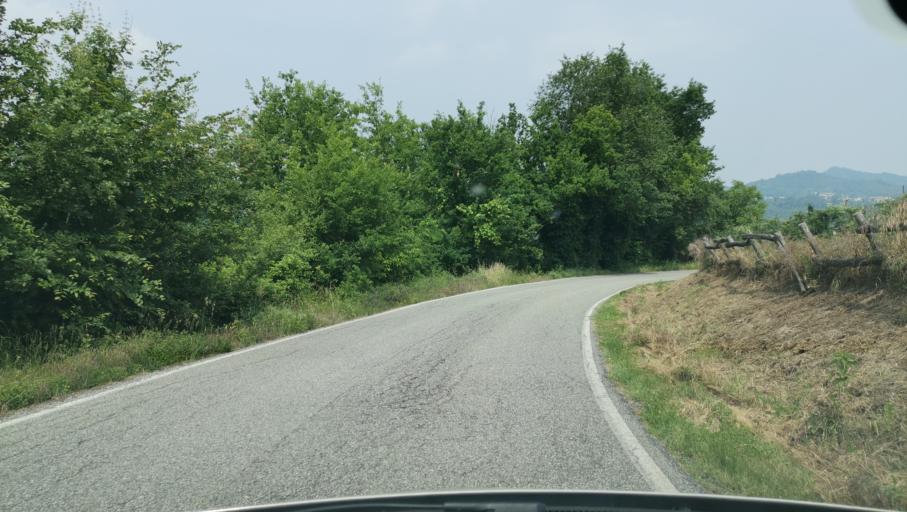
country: IT
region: Piedmont
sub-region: Provincia di Alessandria
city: Villadeati
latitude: 45.0826
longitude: 8.1797
